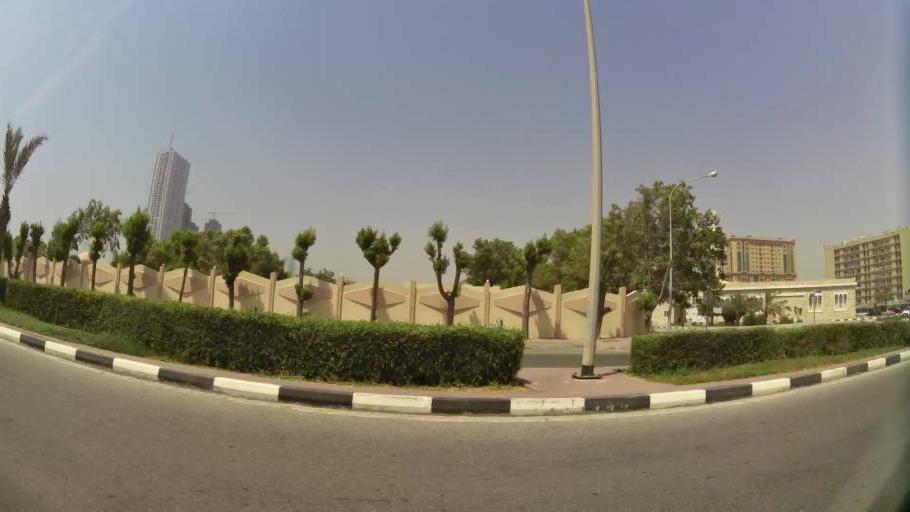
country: AE
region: Ajman
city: Ajman
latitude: 25.3979
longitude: 55.4295
